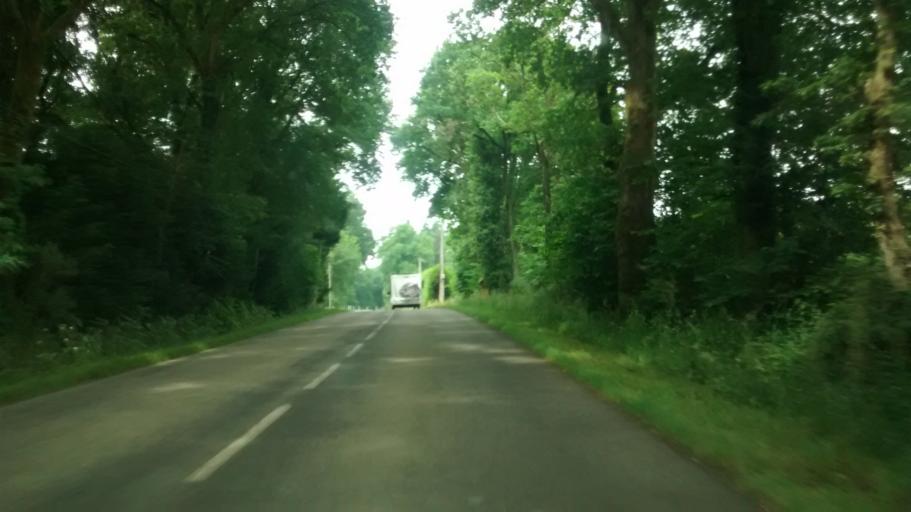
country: FR
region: Brittany
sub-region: Departement du Morbihan
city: Caro
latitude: 47.8321
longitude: -2.3357
